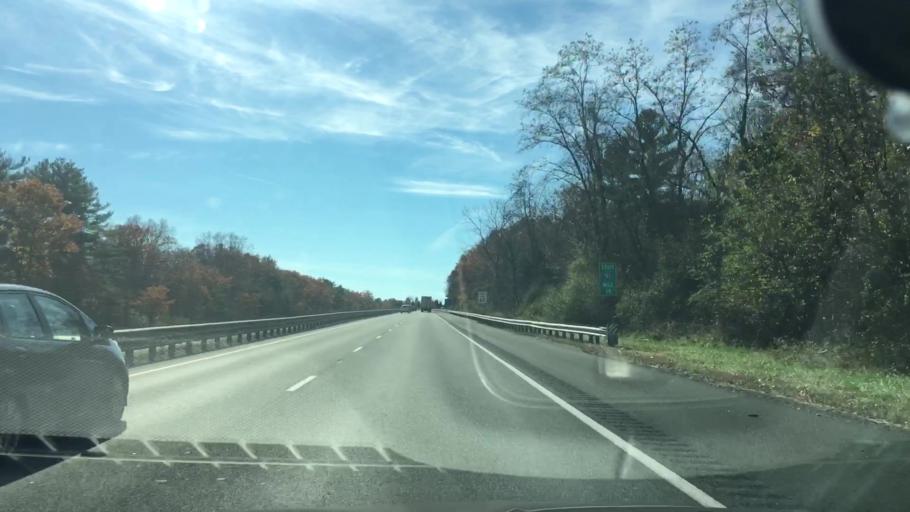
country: US
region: Massachusetts
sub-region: Hampshire County
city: South Hadley
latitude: 42.2635
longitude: -72.6143
